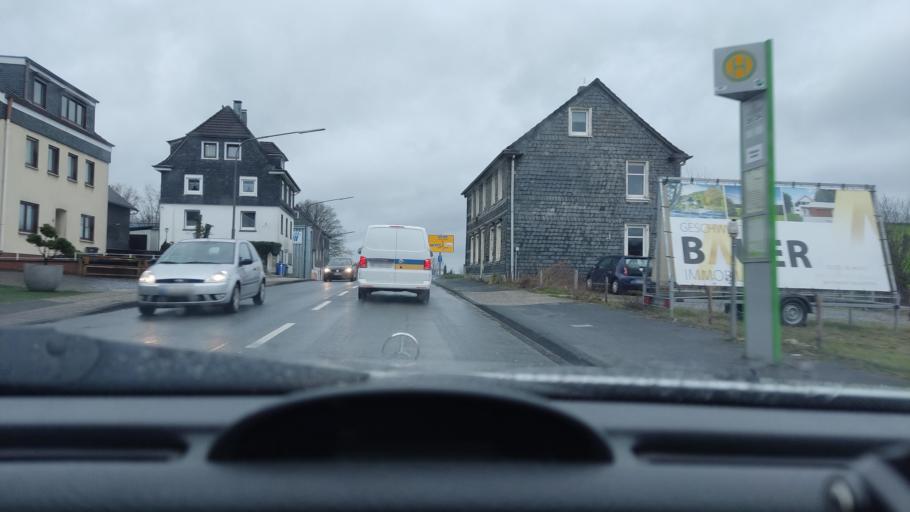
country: DE
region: North Rhine-Westphalia
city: Wermelskirchen
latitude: 51.1361
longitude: 7.2013
